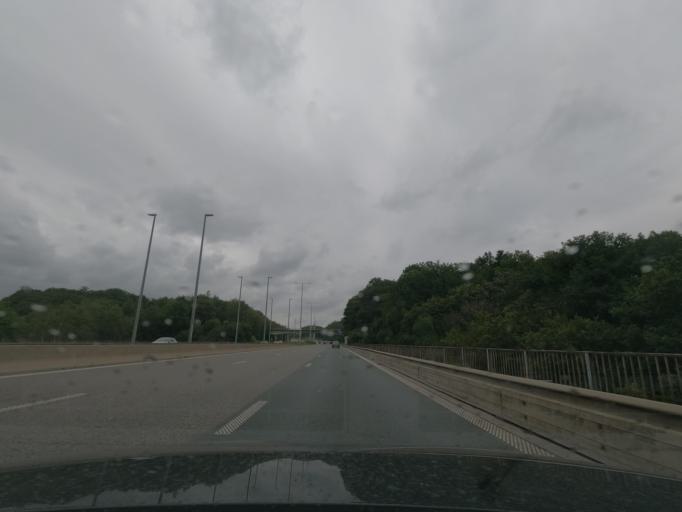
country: BE
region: Wallonia
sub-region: Province du Hainaut
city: Courcelles
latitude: 50.4746
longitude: 4.4030
